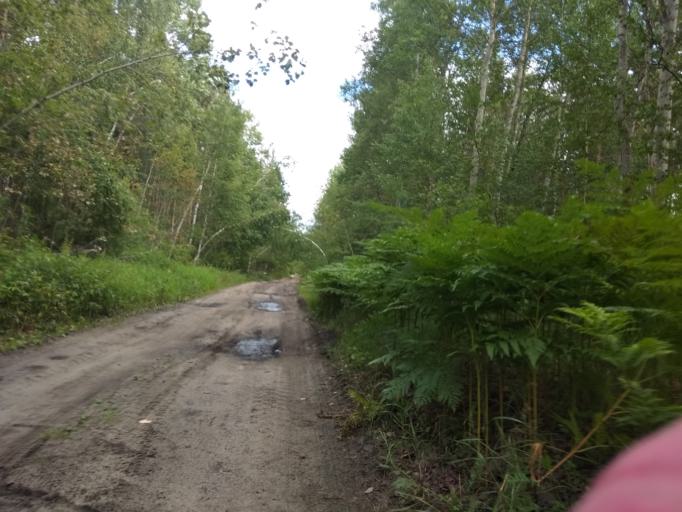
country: RU
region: Moskovskaya
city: Misheronskiy
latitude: 55.7091
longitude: 39.7327
